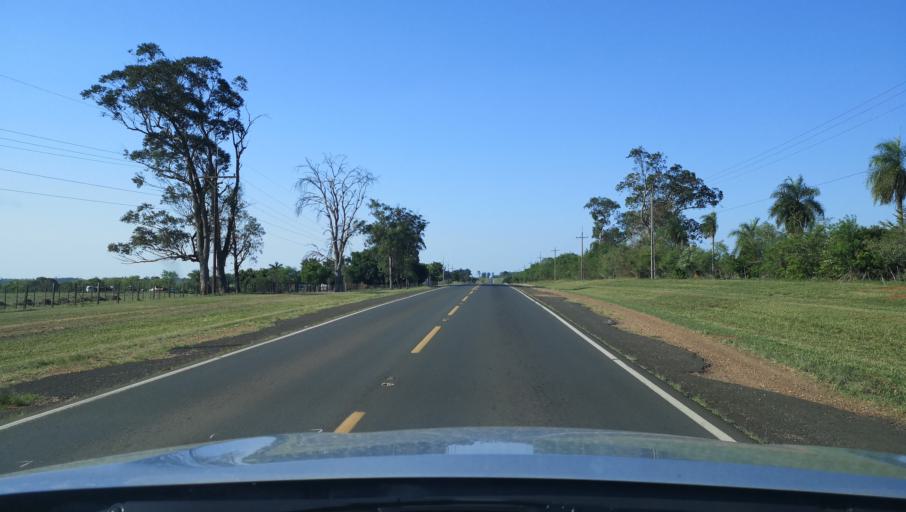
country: PY
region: Misiones
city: Santa Maria
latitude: -26.8230
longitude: -57.0275
